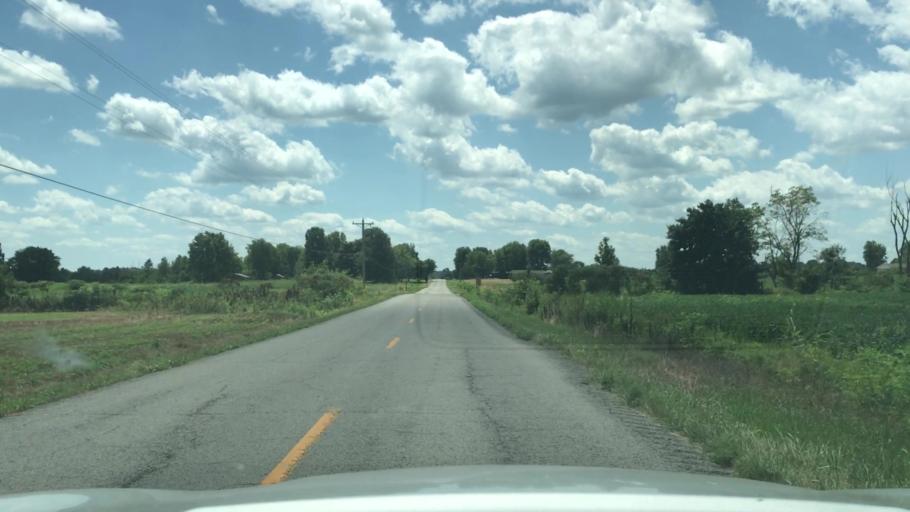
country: US
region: Kentucky
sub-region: Muhlenberg County
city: Greenville
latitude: 37.1589
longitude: -87.2532
